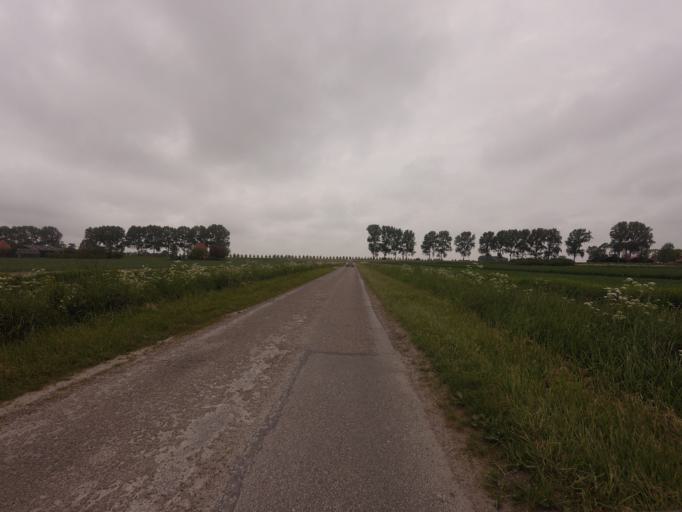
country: NL
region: South Holland
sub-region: Gemeente Goeree-Overflakkee
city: Dirksland
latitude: 51.7176
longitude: 4.1136
